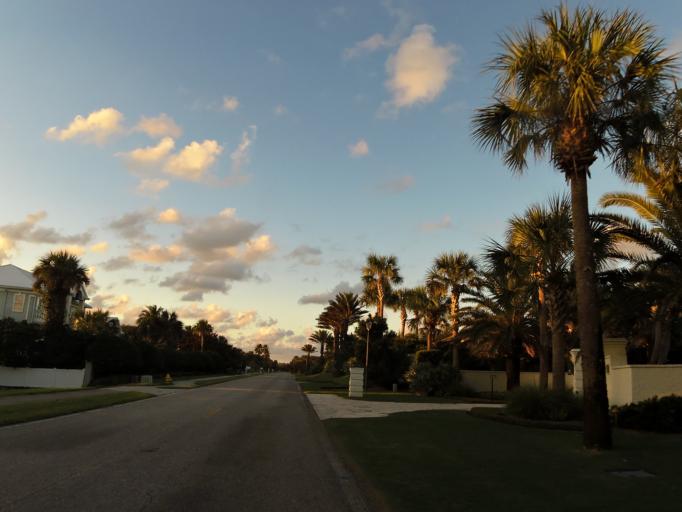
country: US
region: Florida
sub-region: Saint Johns County
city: Sawgrass
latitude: 30.1863
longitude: -81.3635
